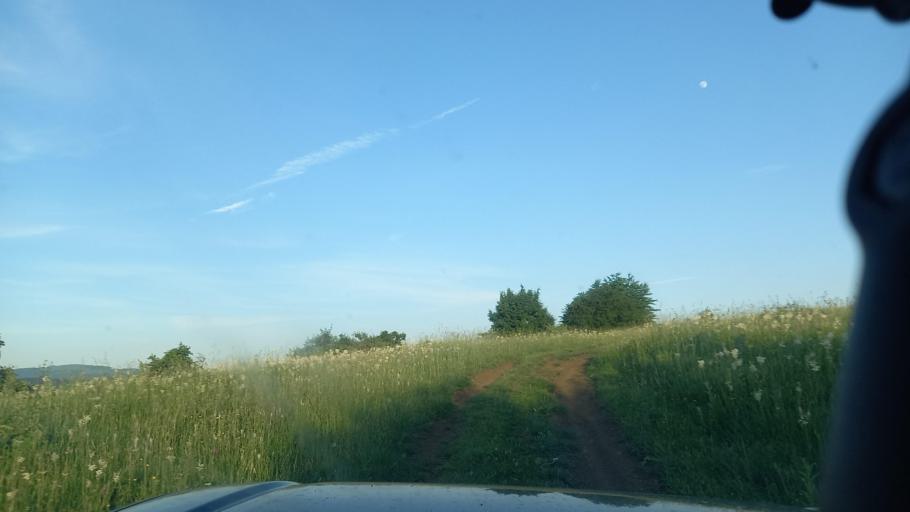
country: RU
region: Karachayevo-Cherkesiya
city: Kurdzhinovo
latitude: 44.1254
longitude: 41.0882
